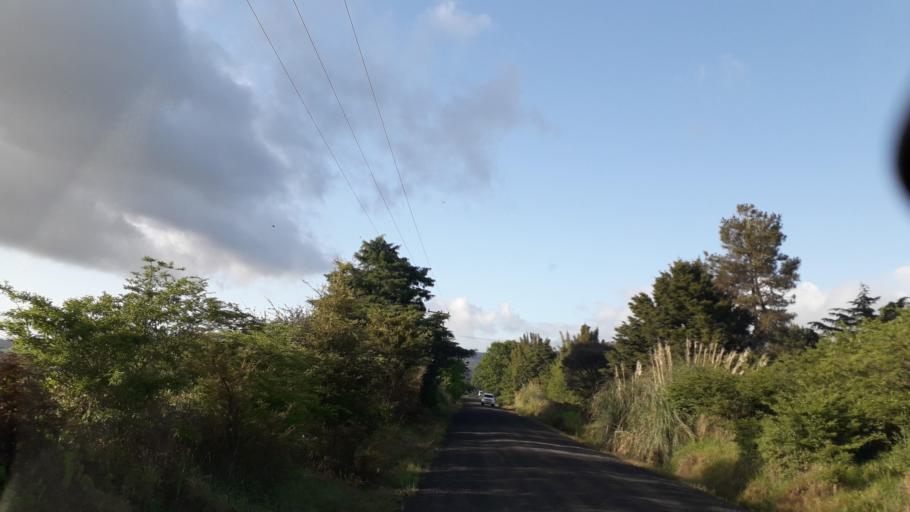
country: NZ
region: Northland
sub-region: Far North District
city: Waimate North
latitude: -35.4954
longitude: 173.6994
